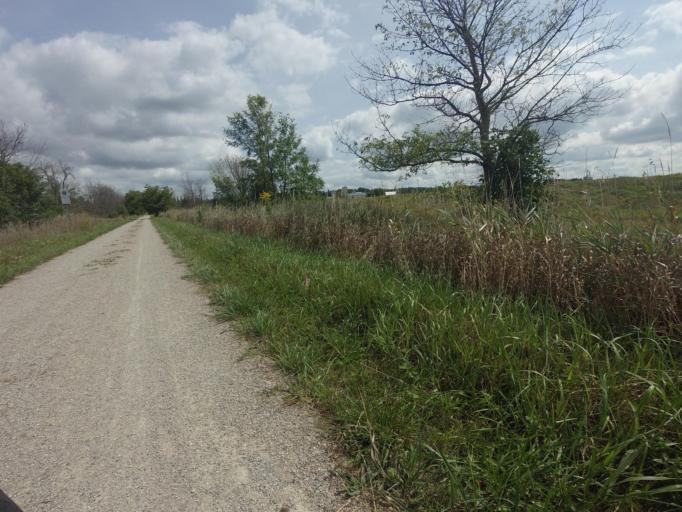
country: CA
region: Ontario
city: North Perth
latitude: 43.5675
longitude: -80.9326
